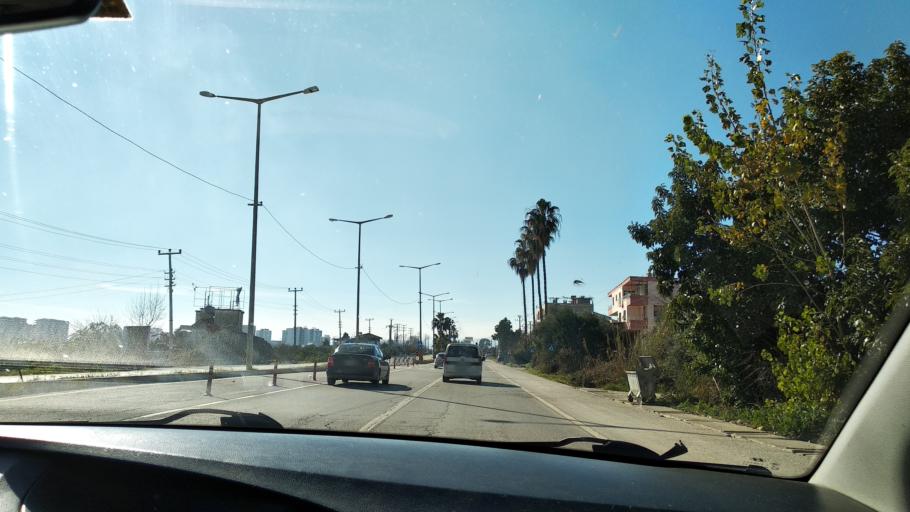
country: TR
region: Mersin
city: Tomuk
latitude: 36.6520
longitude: 34.3797
